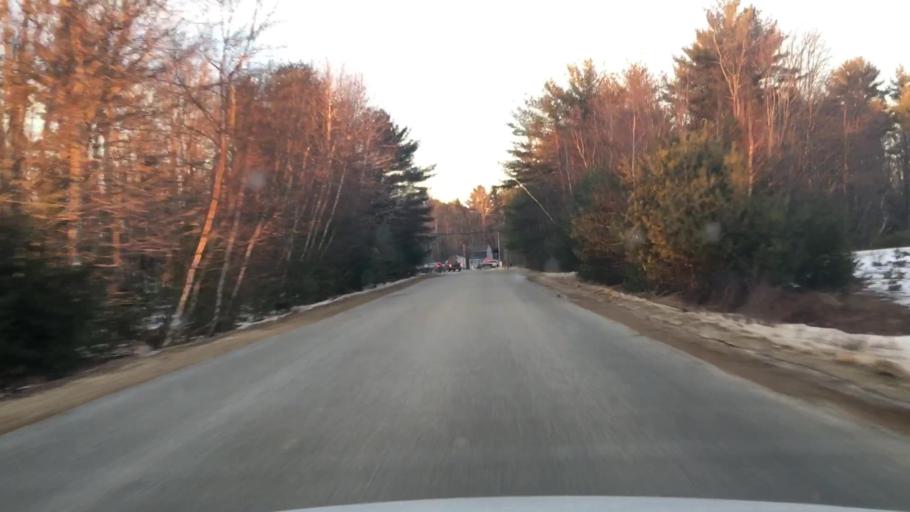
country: US
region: Maine
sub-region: York County
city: Lebanon
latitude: 43.3793
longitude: -70.8775
